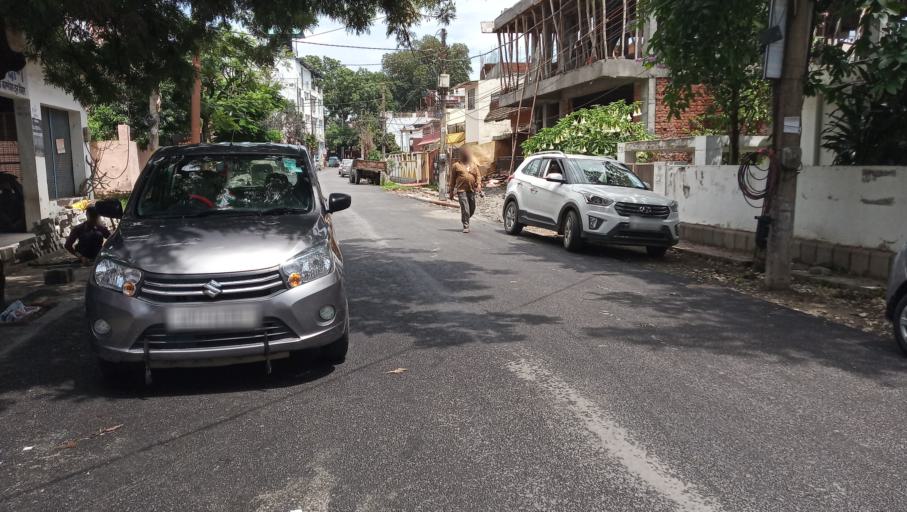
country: IN
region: Uttarakhand
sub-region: Dehradun
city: Dehradun
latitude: 30.3647
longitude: 78.0679
